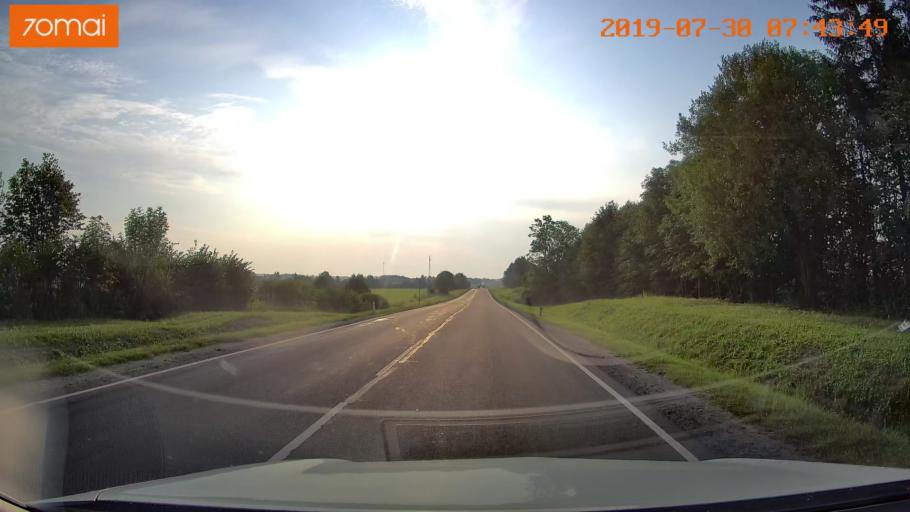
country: RU
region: Kaliningrad
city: Gvardeysk
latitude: 54.6494
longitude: 21.3120
